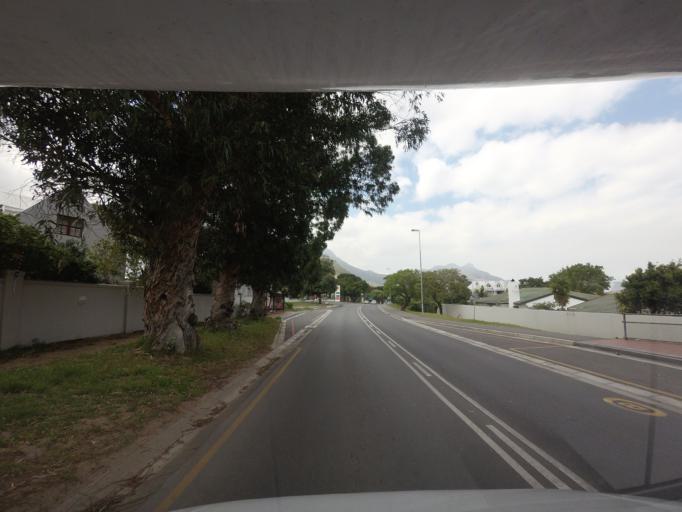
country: ZA
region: Western Cape
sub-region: City of Cape Town
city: Constantia
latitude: -34.0395
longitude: 18.3589
